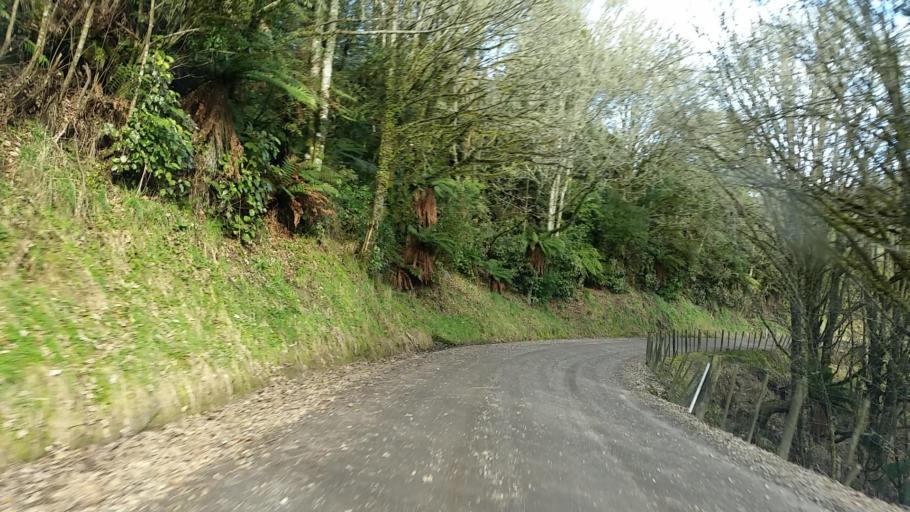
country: NZ
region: Taranaki
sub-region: New Plymouth District
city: Waitara
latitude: -39.1619
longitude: 174.5746
